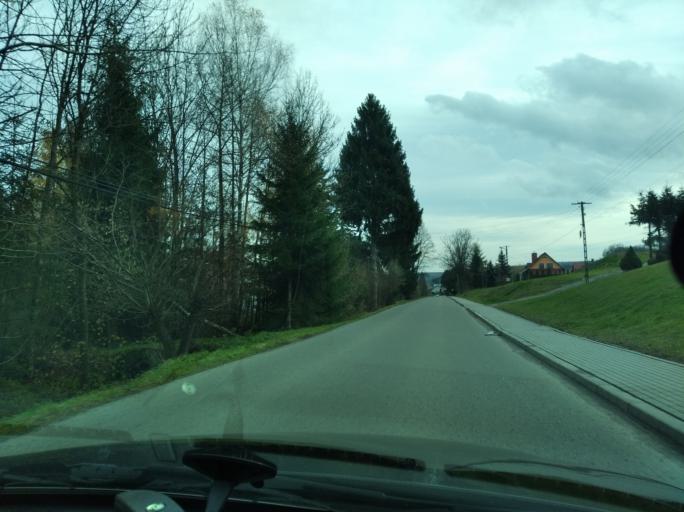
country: PL
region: Subcarpathian Voivodeship
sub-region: Powiat strzyzowski
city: Strzyzow
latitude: 49.9387
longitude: 21.7565
